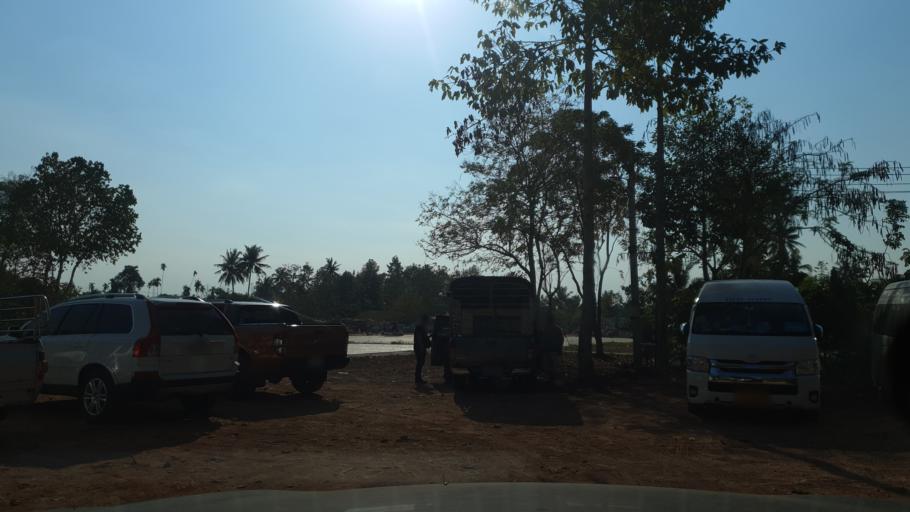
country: TH
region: Samut Songkhram
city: Bang Khon Thi
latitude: 13.4451
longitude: 99.9410
